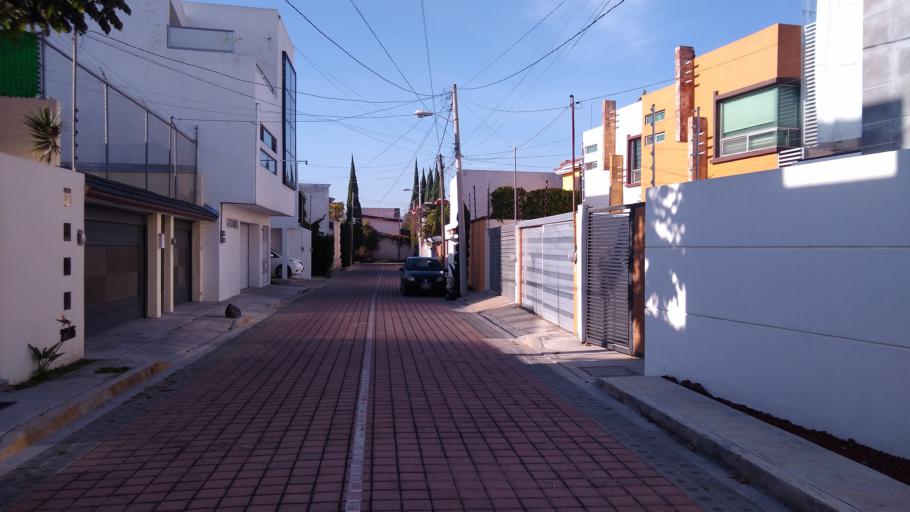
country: MX
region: Puebla
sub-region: San Pedro Cholula
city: Santiago Momoxpan
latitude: 19.0587
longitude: -98.2716
